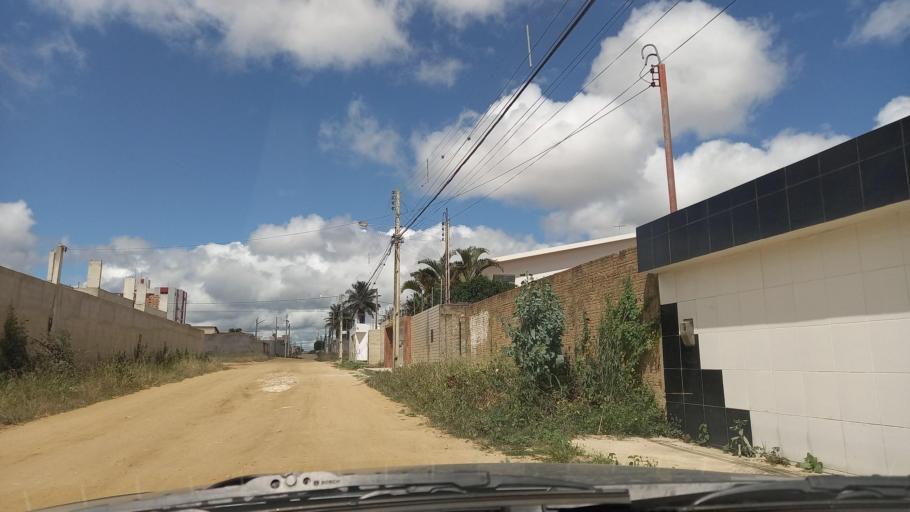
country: BR
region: Pernambuco
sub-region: Caruaru
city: Caruaru
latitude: -8.2552
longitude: -35.9792
